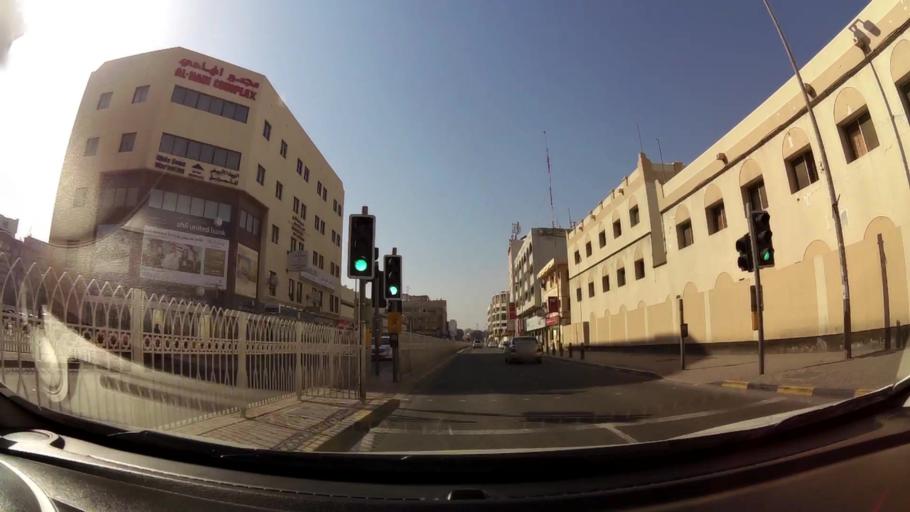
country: BH
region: Manama
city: Manama
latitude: 26.2279
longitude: 50.5880
